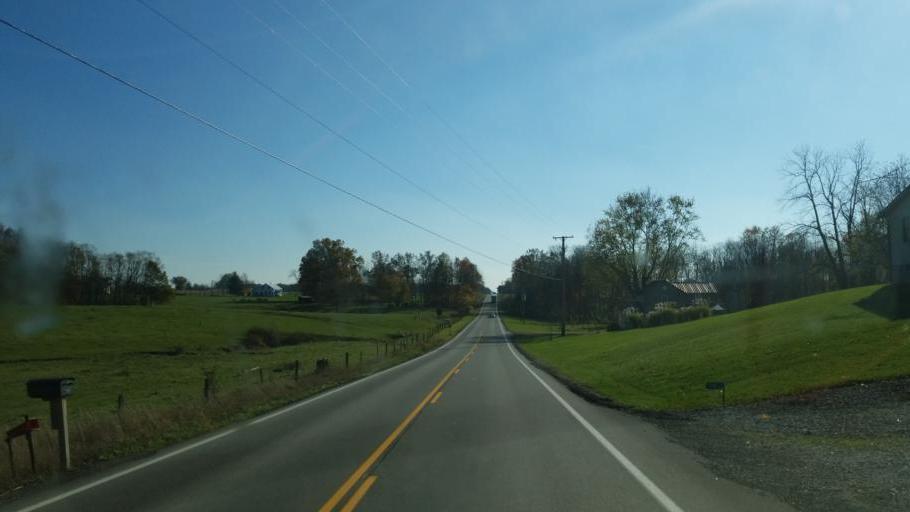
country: US
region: Ohio
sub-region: Wayne County
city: West Salem
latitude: 40.9264
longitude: -82.2146
